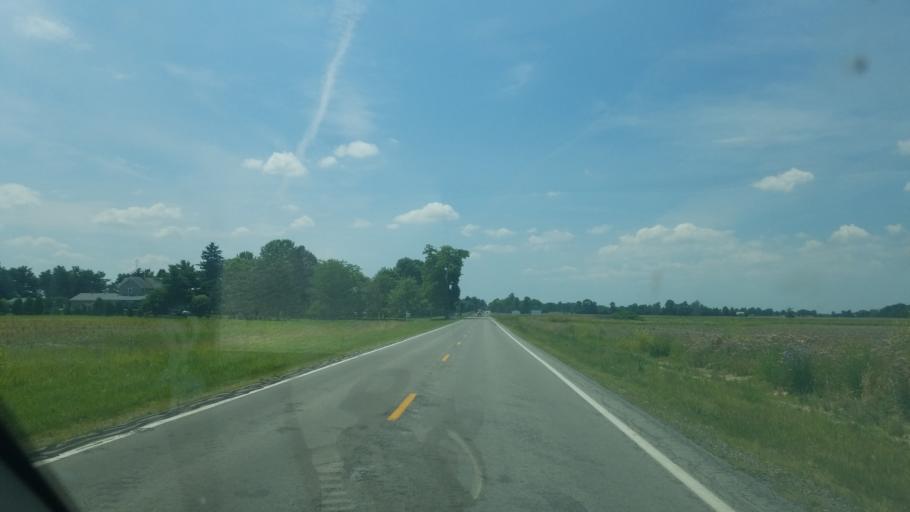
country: US
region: Ohio
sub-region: Hardin County
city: Ada
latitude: 40.7766
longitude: -83.7971
